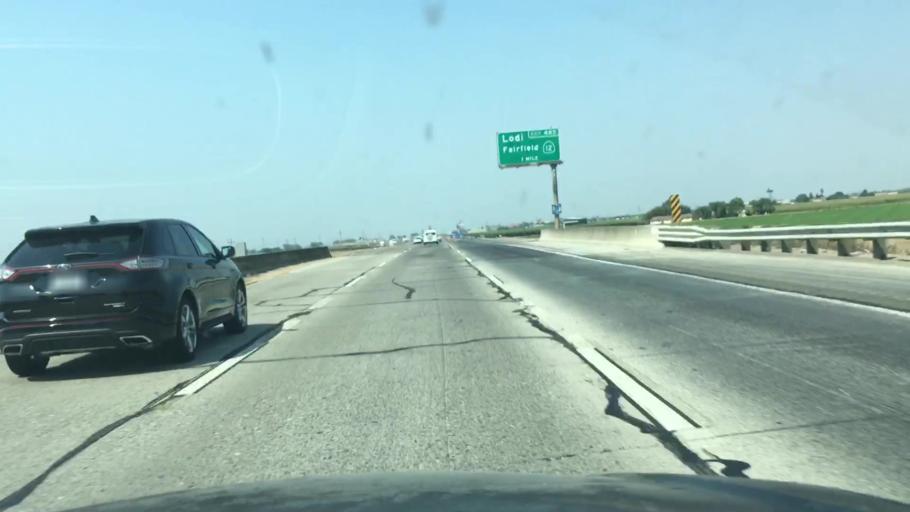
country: US
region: California
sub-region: San Joaquin County
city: Woodbridge
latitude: 38.0961
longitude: -121.3861
